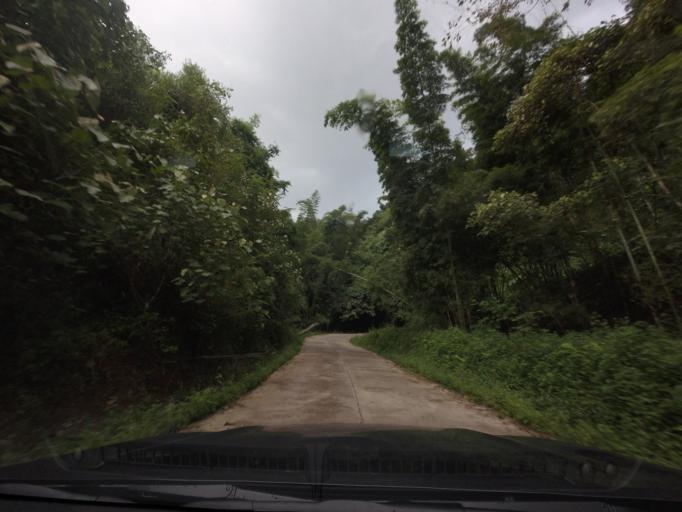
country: TH
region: Nan
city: Bo Kluea
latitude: 19.3517
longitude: 101.1619
